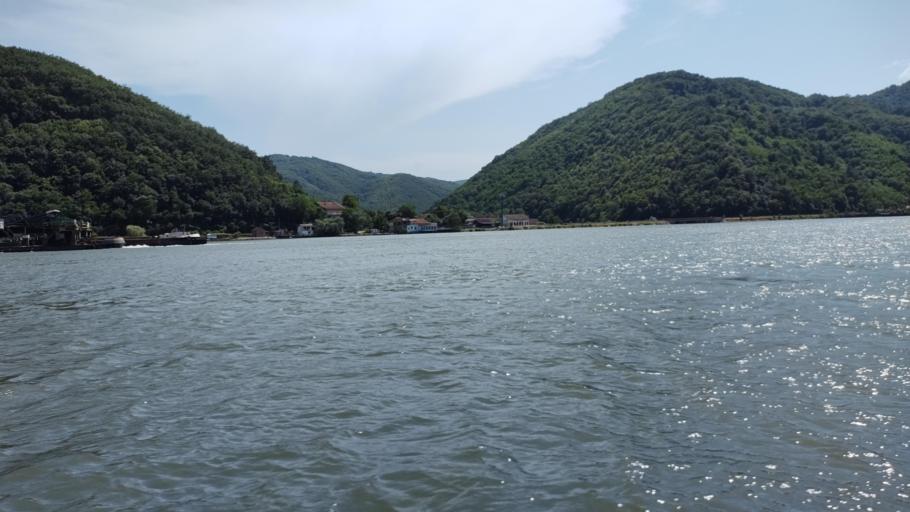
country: RS
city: Radenka
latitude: 44.6602
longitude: 21.7676
